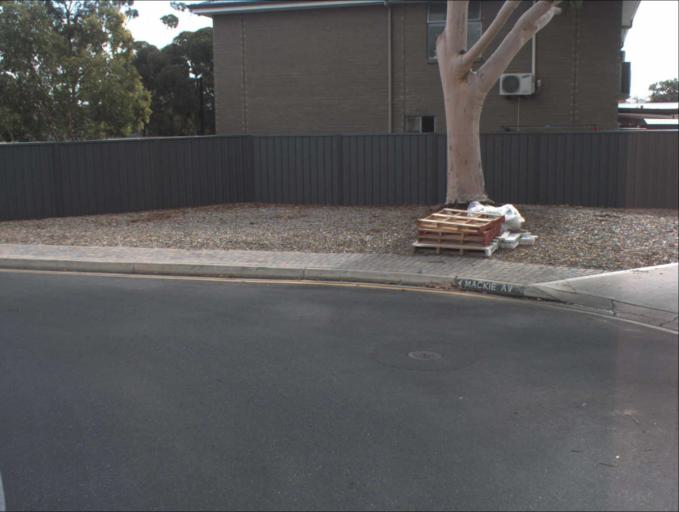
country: AU
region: South Australia
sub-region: Port Adelaide Enfield
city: Blair Athol
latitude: -34.8693
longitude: 138.5857
